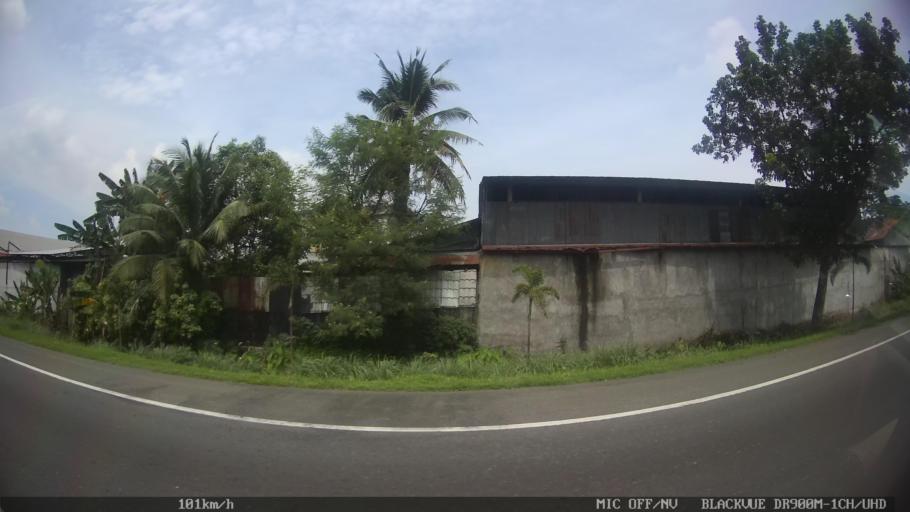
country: ID
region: North Sumatra
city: Labuhan Deli
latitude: 3.7055
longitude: 98.6815
